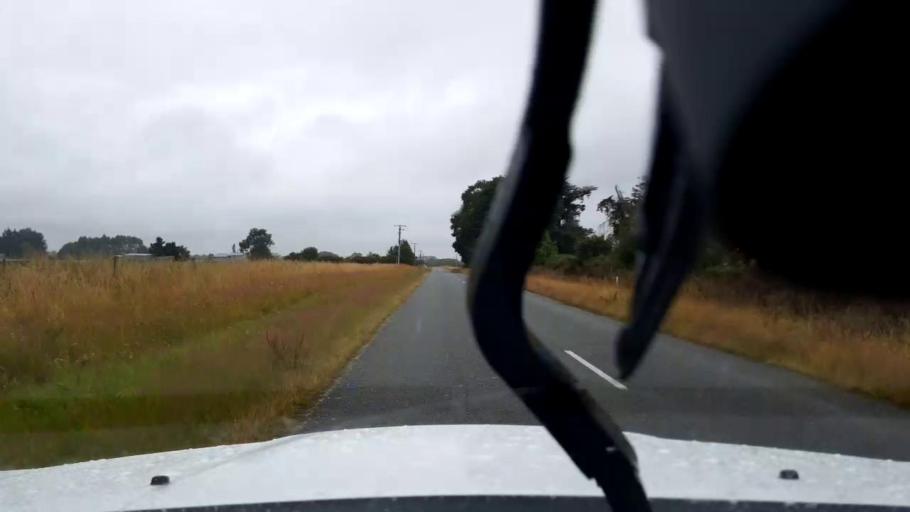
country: NZ
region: Canterbury
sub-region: Timaru District
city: Pleasant Point
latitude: -44.2542
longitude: 171.2414
